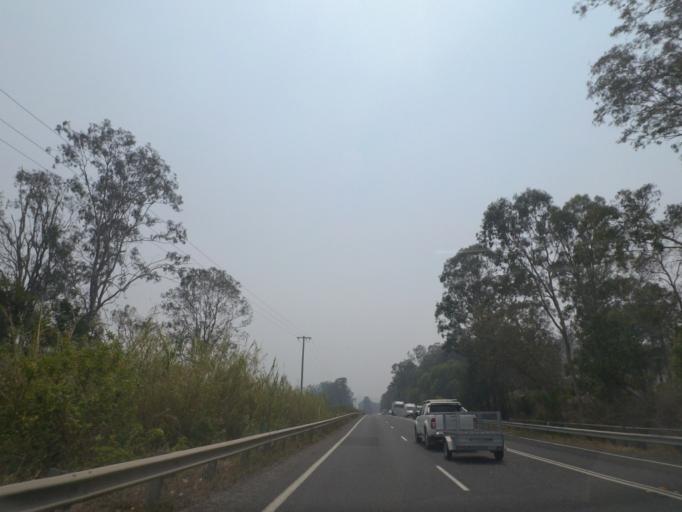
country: AU
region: New South Wales
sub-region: Clarence Valley
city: Maclean
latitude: -29.5589
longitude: 153.1501
